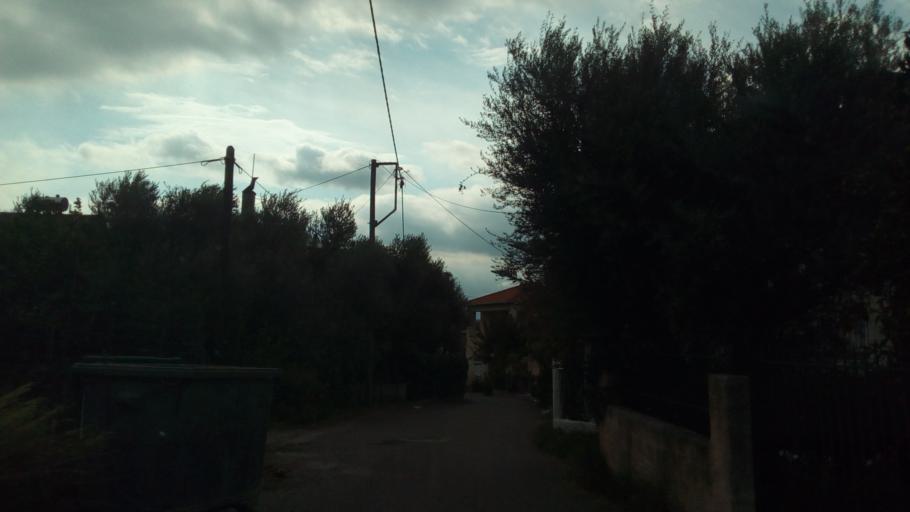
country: GR
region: West Greece
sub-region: Nomos Achaias
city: Kamarai
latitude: 38.3921
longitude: 22.0112
